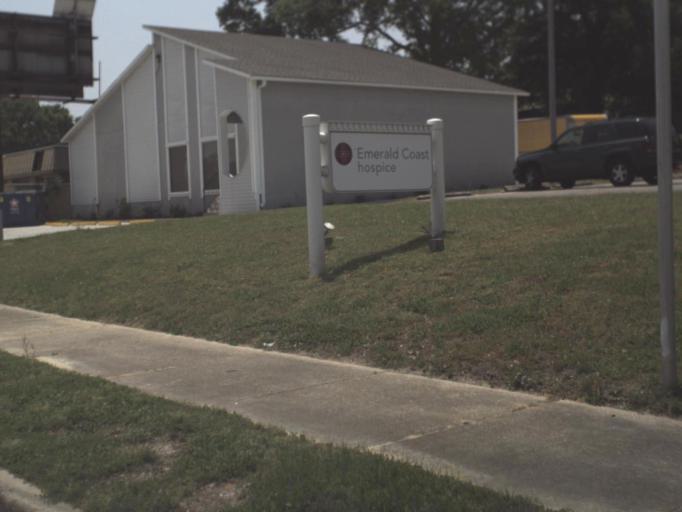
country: US
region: Florida
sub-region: Escambia County
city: Pensacola
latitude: 30.4287
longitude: -87.2191
